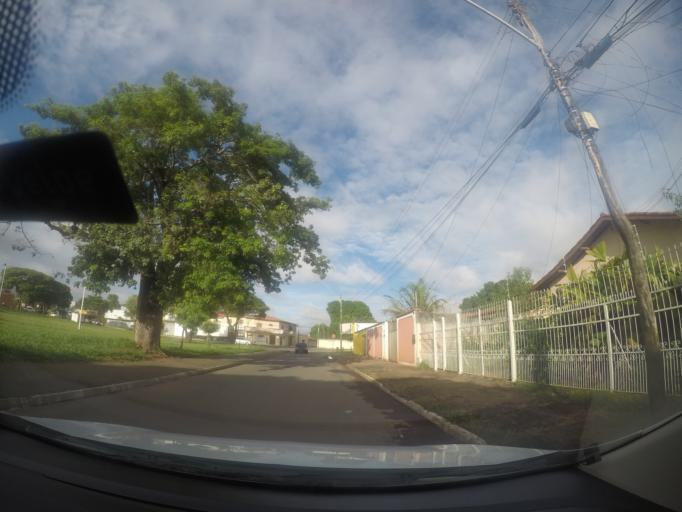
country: BR
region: Goias
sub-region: Goiania
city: Goiania
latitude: -16.6885
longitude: -49.3104
